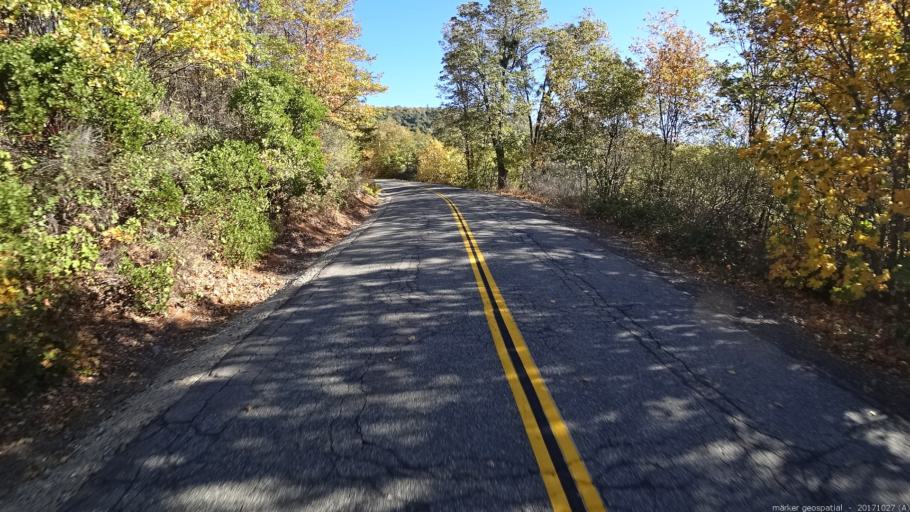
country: US
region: California
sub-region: Shasta County
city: Burney
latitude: 40.8532
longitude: -121.9090
